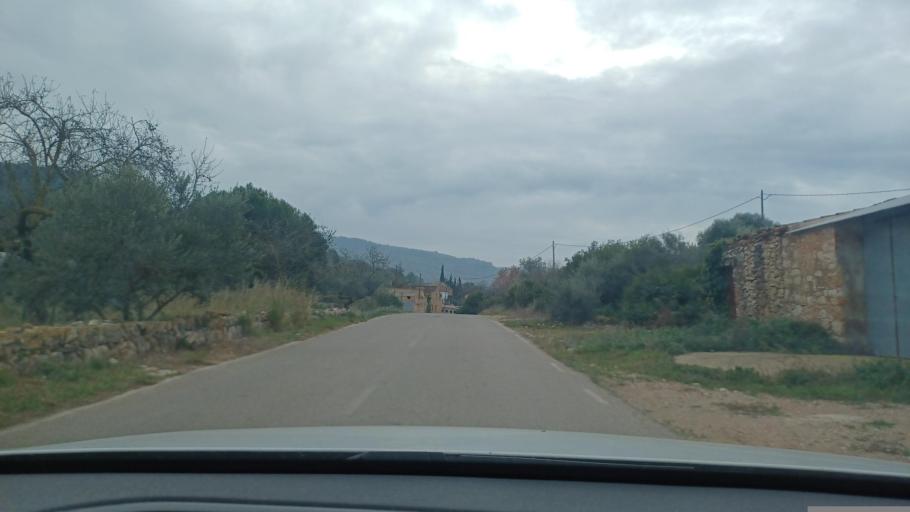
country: ES
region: Catalonia
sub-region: Provincia de Tarragona
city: Santa Barbara
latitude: 40.6607
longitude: 0.4640
